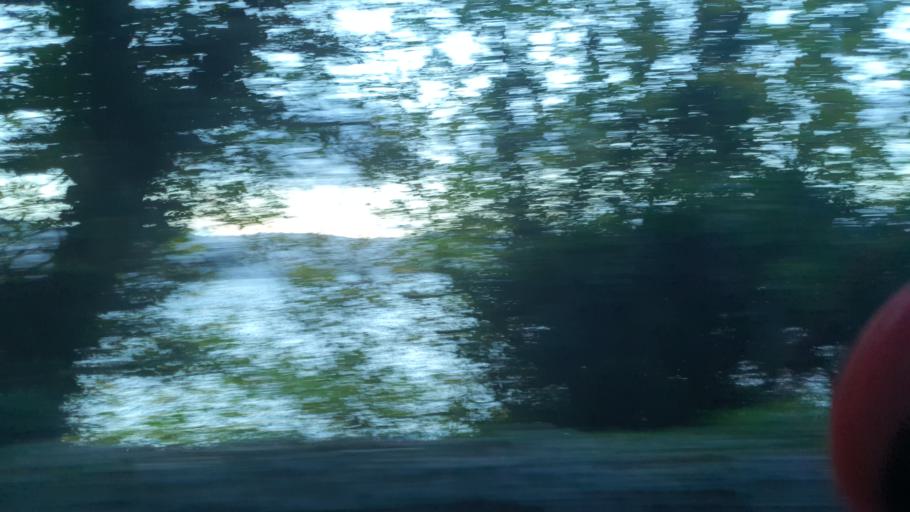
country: GB
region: Northern Ireland
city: Rostrevor
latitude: 54.0872
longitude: -6.1898
